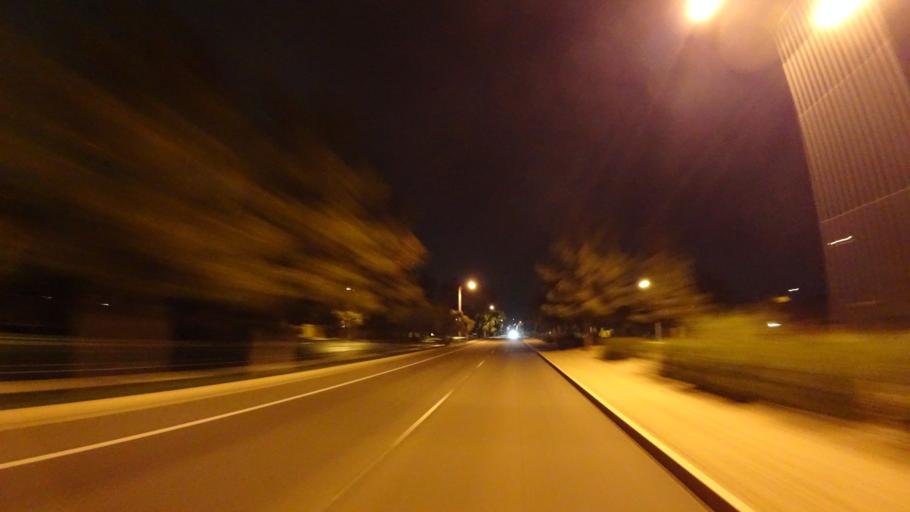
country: US
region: Arizona
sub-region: Maricopa County
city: Sun Lakes
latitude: 33.2541
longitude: -111.8606
